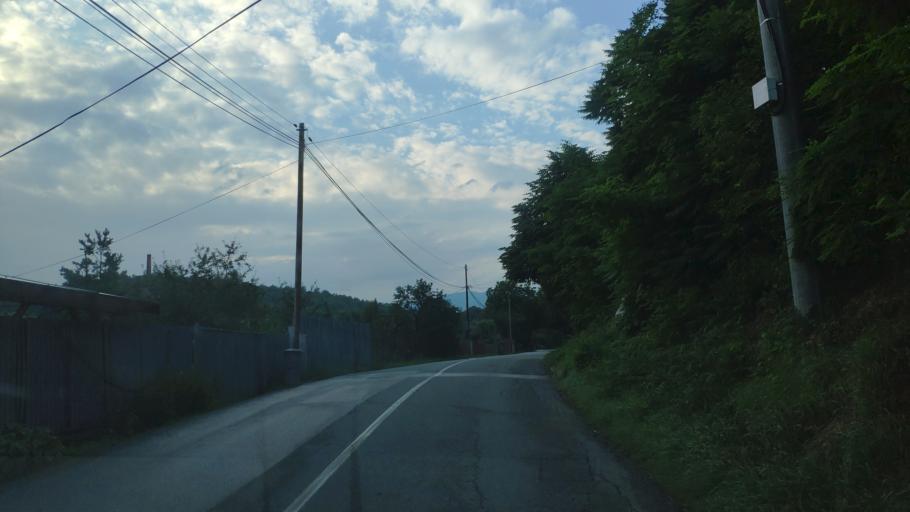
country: SK
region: Kosicky
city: Moldava nad Bodvou
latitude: 48.6850
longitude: 20.9752
